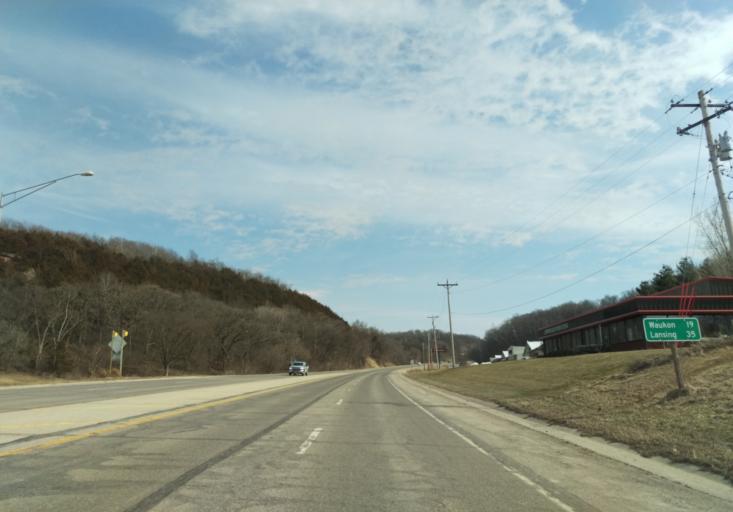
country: US
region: Iowa
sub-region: Winneshiek County
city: Decorah
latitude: 43.2877
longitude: -91.7536
